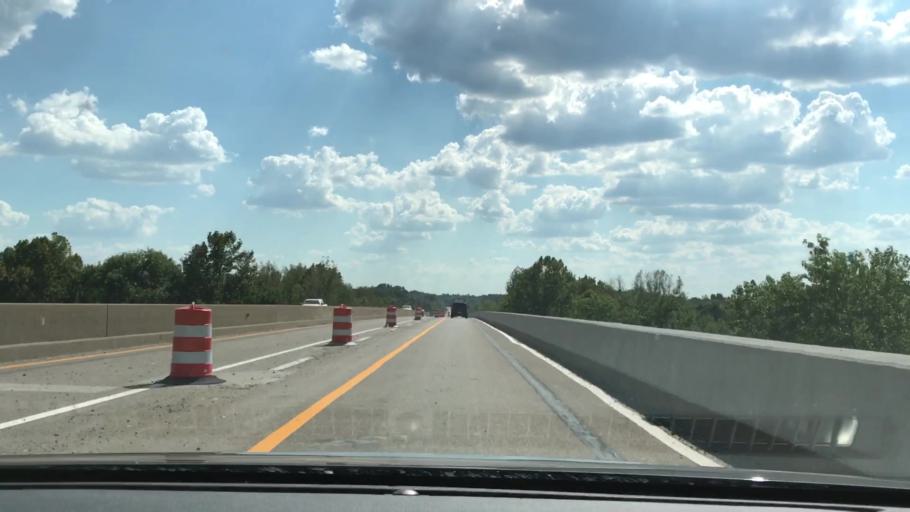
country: US
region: Kentucky
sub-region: Ohio County
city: Oak Grove
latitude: 37.2829
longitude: -86.7435
